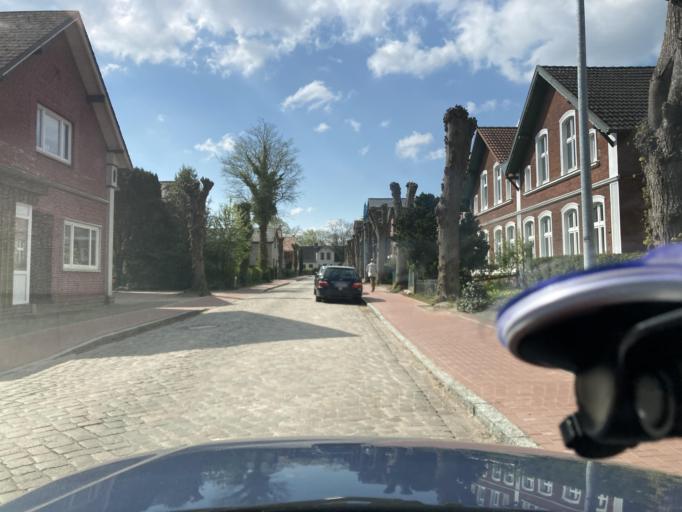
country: DE
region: Schleswig-Holstein
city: Meldorf
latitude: 54.0878
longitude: 9.0762
